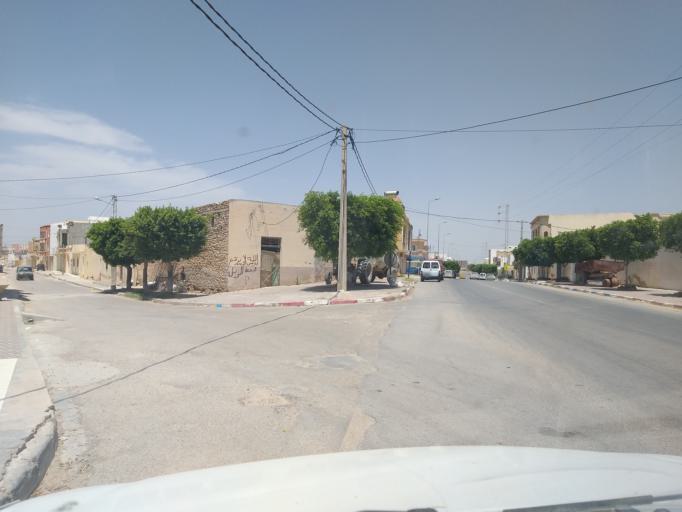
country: TN
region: Al Mahdiyah
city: El Jem
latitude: 35.2950
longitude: 10.6997
